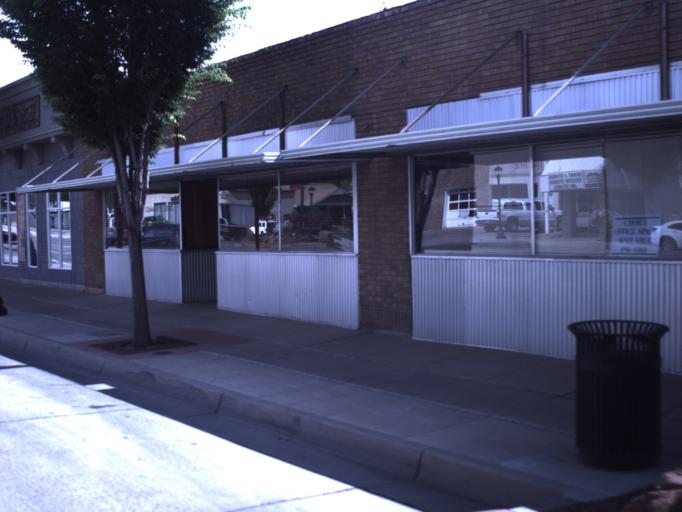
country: US
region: Utah
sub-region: Sevier County
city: Richfield
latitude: 38.7702
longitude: -112.0847
